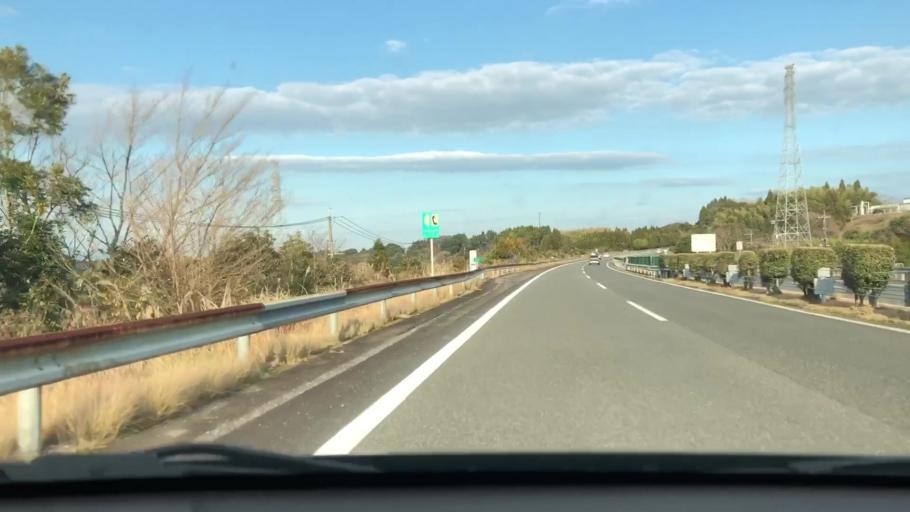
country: JP
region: Miyazaki
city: Miyazaki-shi
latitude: 31.8277
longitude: 131.3112
